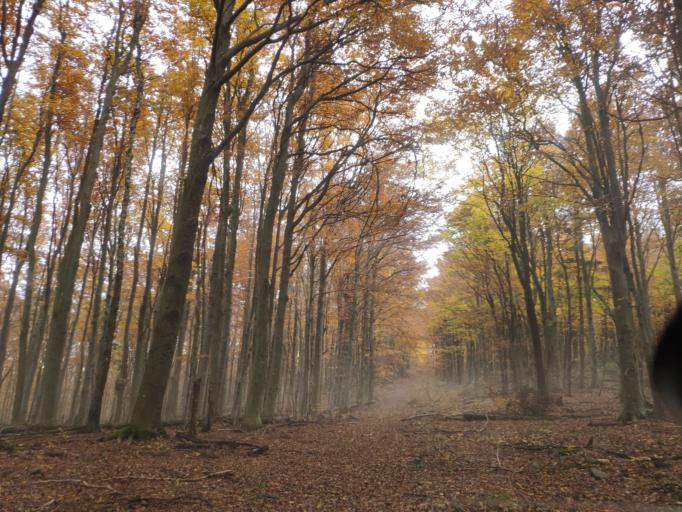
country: SK
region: Kosicky
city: Medzev
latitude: 48.7356
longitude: 21.0028
